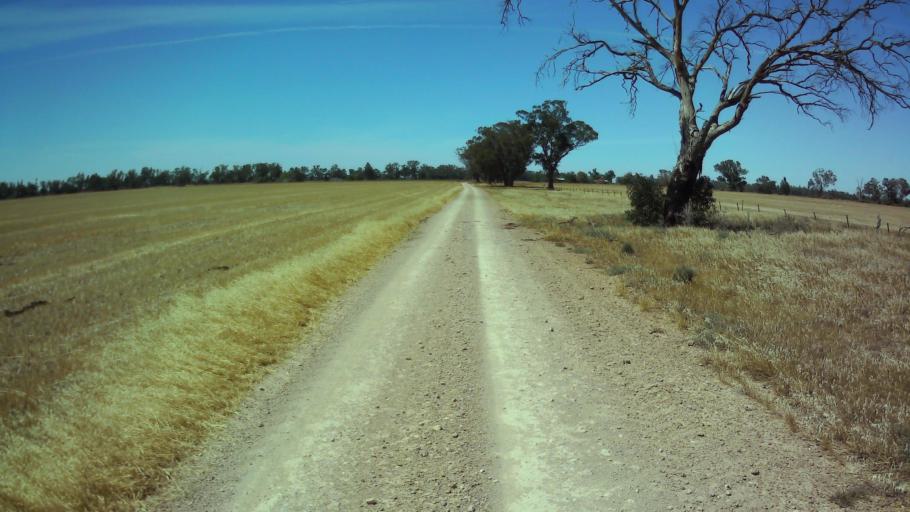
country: AU
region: New South Wales
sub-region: Weddin
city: Grenfell
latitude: -34.0355
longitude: 147.8896
